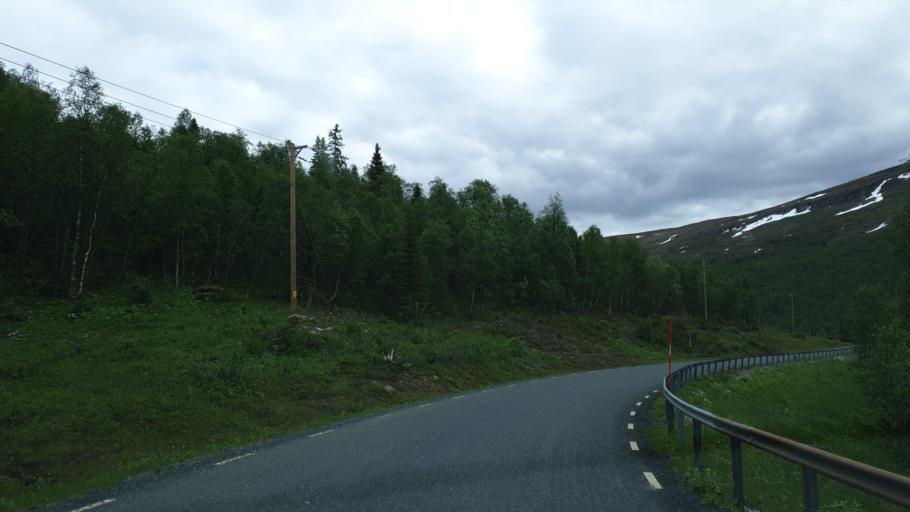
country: NO
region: Nordland
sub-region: Hattfjelldal
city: Hattfjelldal
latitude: 65.4283
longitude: 14.6007
